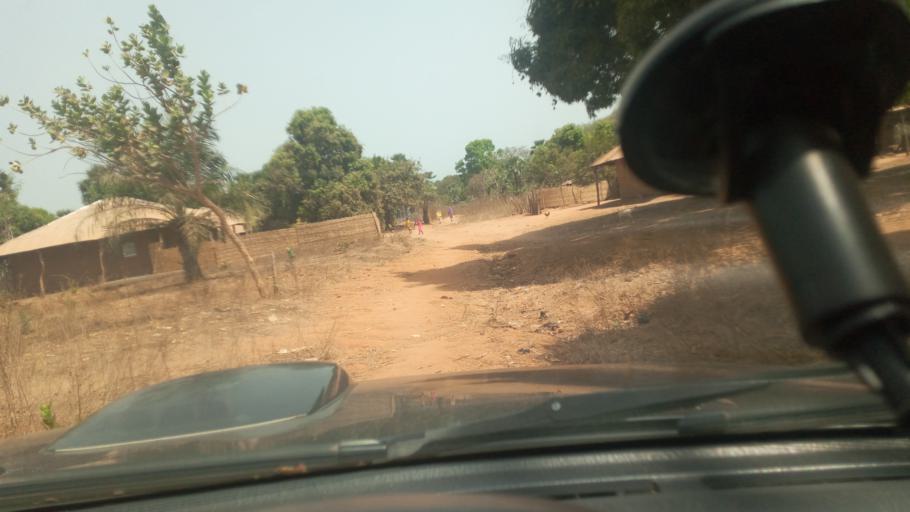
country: SN
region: Sedhiou
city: Sedhiou
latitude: 12.4454
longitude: -15.6160
